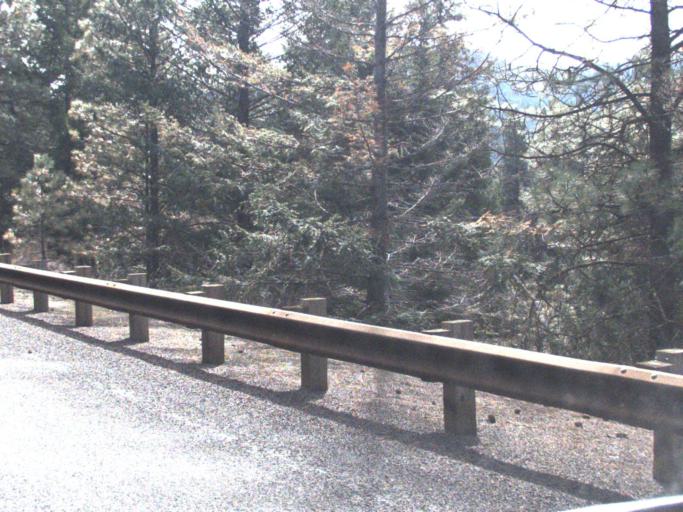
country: US
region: Washington
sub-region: Kittitas County
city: Cle Elum
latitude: 46.9284
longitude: -121.0474
